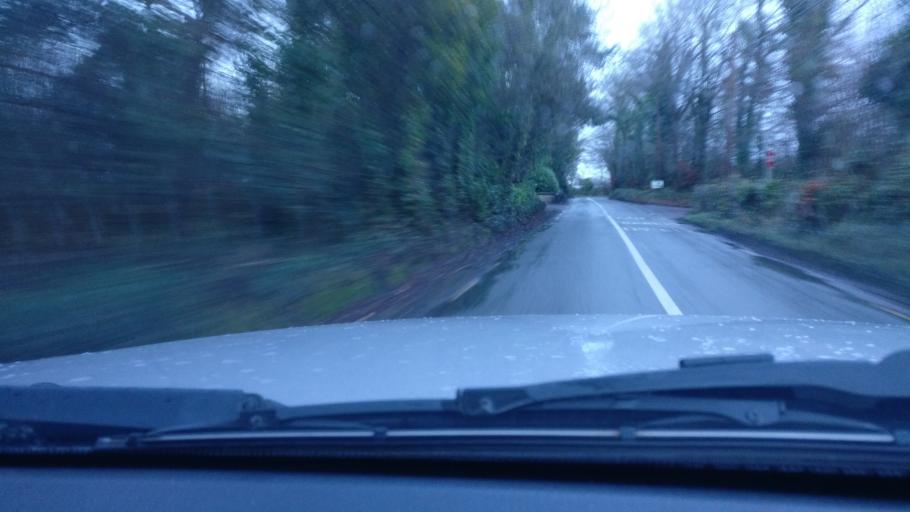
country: IE
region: Connaught
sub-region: County Galway
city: Ballinasloe
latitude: 53.2763
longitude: -8.2430
